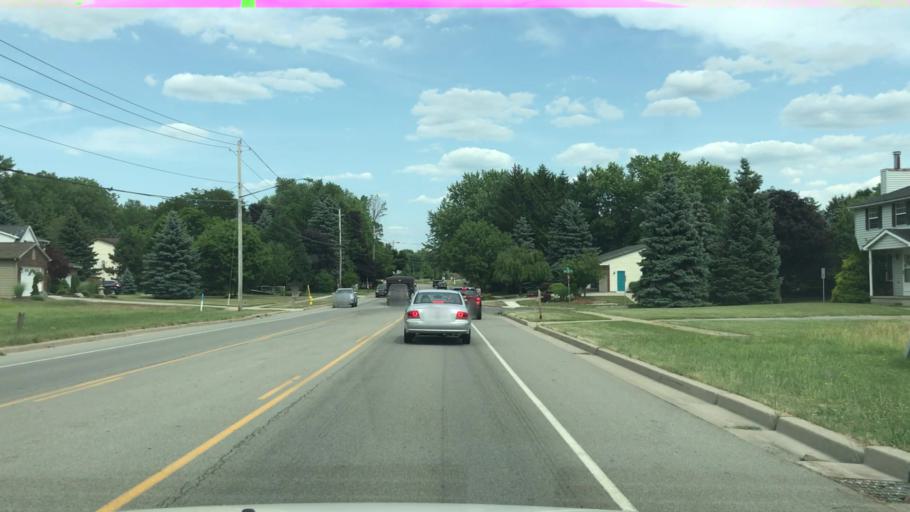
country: US
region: New York
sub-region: Erie County
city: Cheektowaga
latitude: 42.8805
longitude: -78.7240
